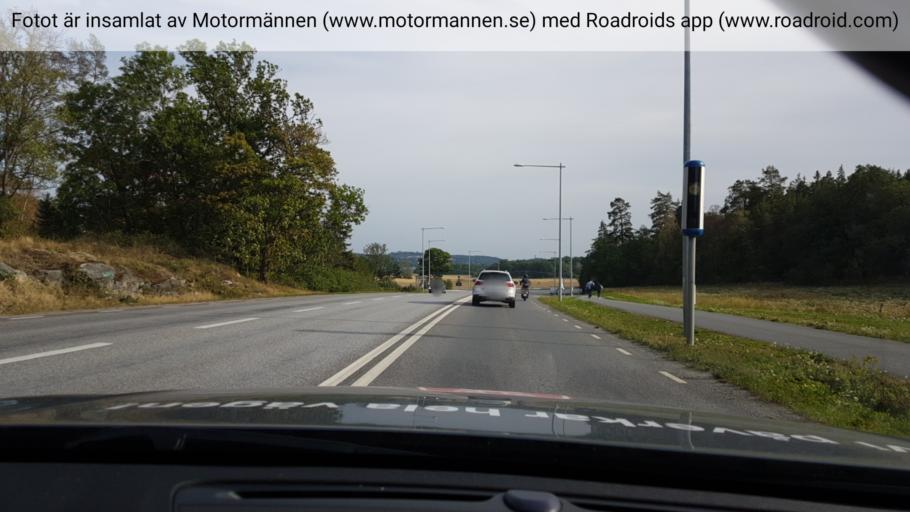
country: SE
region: Stockholm
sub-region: Ekero Kommun
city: Ekeroe
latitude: 59.3114
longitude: 17.8606
